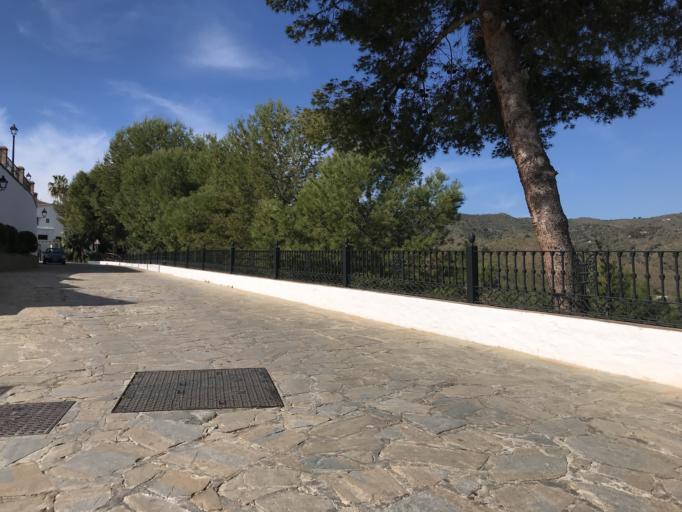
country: ES
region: Andalusia
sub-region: Provincia de Malaga
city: Valdes
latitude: 36.7626
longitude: -4.2146
